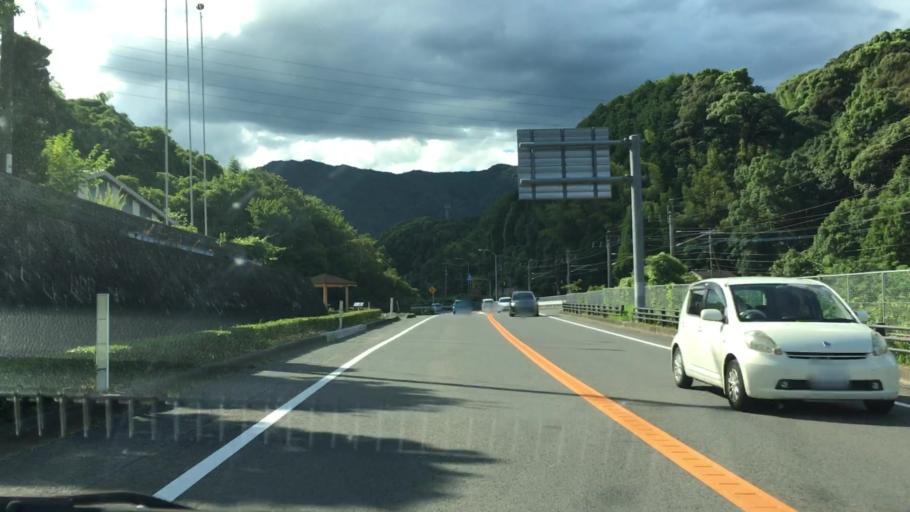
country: JP
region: Saga Prefecture
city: Imaricho-ko
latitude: 33.1893
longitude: 129.9235
